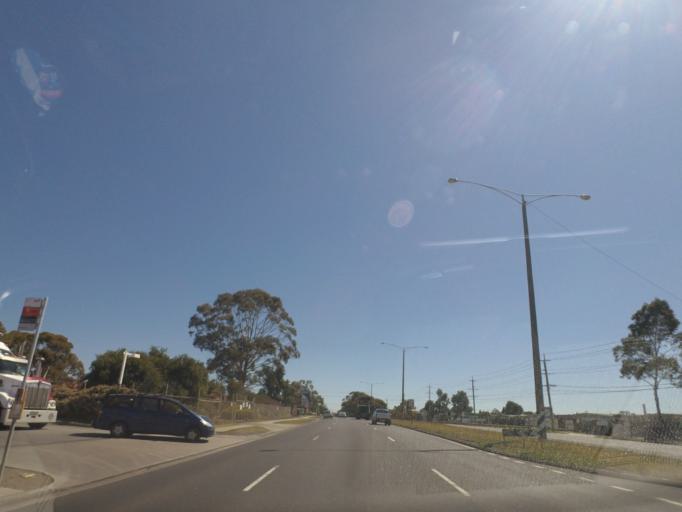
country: AU
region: Victoria
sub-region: Hume
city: Campbellfield
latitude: -37.6739
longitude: 144.9557
